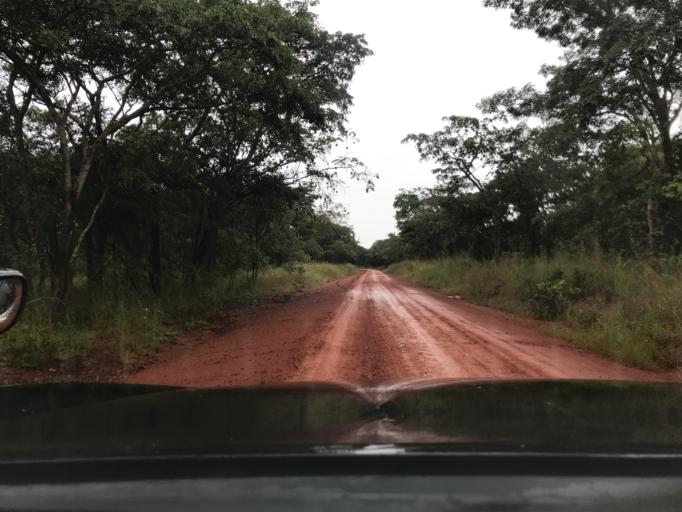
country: TZ
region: Kigoma
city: Uvinza
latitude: -5.2899
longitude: 30.3691
